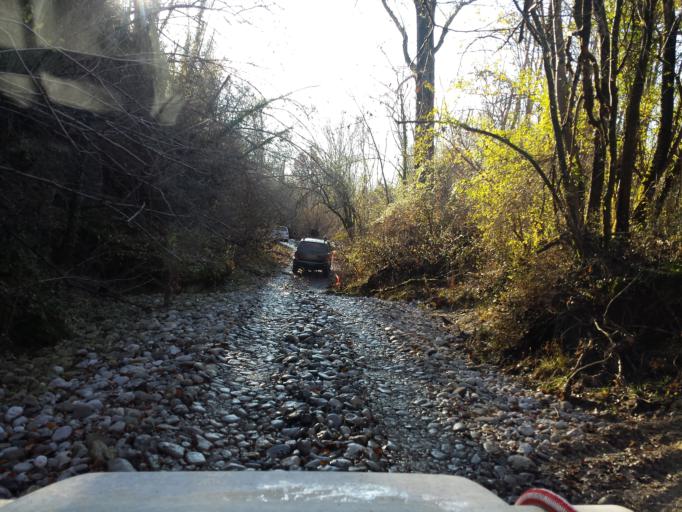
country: IT
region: Friuli Venezia Giulia
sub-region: Provincia di Udine
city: Orsaria
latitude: 46.0252
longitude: 13.3817
